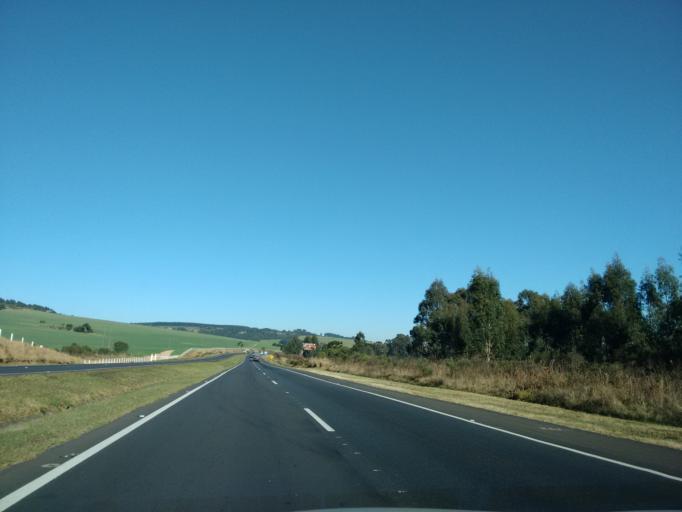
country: BR
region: Parana
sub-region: Palmeira
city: Palmeira
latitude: -25.2598
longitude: -49.9940
